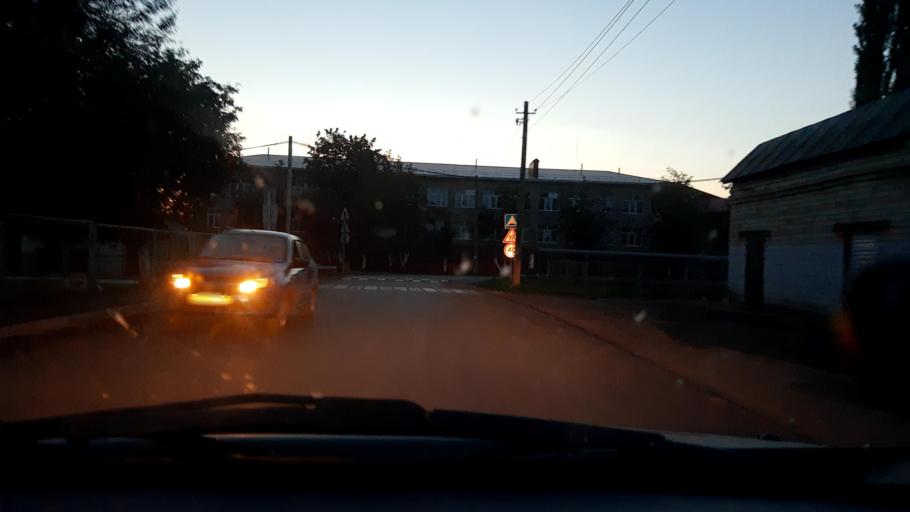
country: RU
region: Bashkortostan
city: Ulukulevo
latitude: 54.4249
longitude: 56.3309
